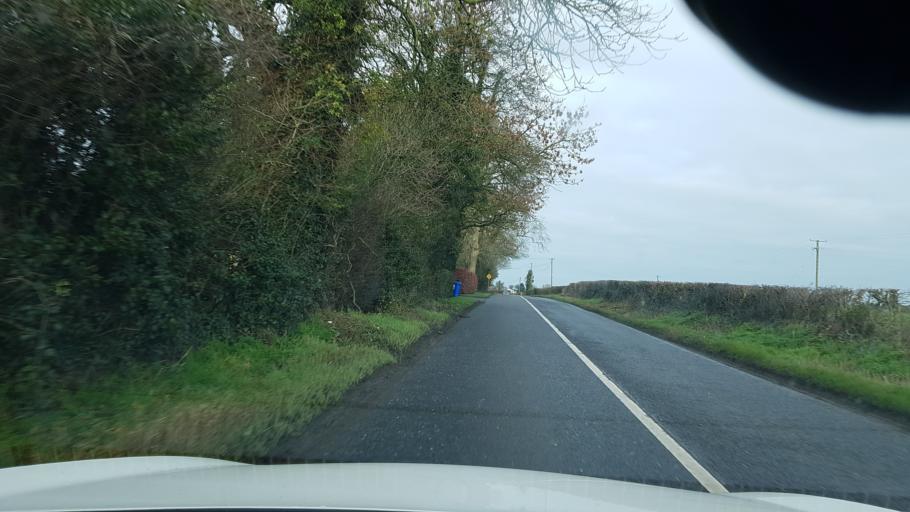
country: IE
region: Leinster
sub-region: An Mhi
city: Navan
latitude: 53.6952
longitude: -6.6767
